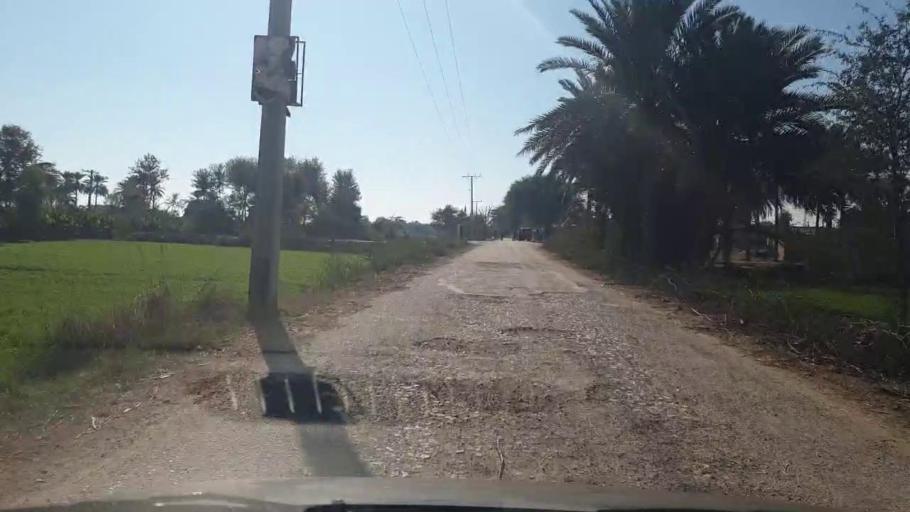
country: PK
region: Sindh
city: Kot Diji
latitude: 27.2754
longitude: 68.6513
